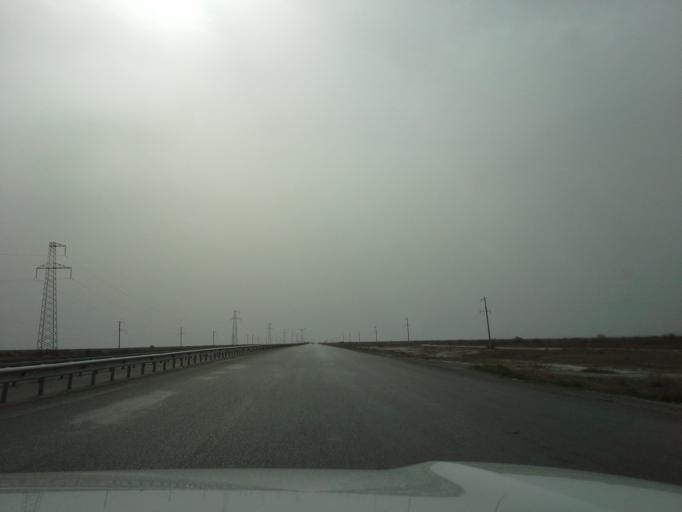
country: TM
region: Ahal
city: Kaka
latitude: 37.5371
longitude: 59.4051
